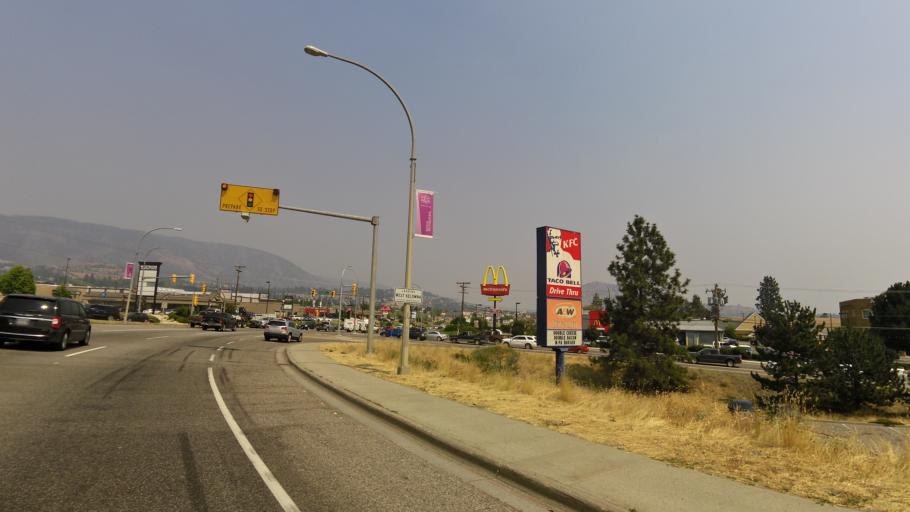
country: CA
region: British Columbia
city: West Kelowna
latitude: 49.8303
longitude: -119.6229
